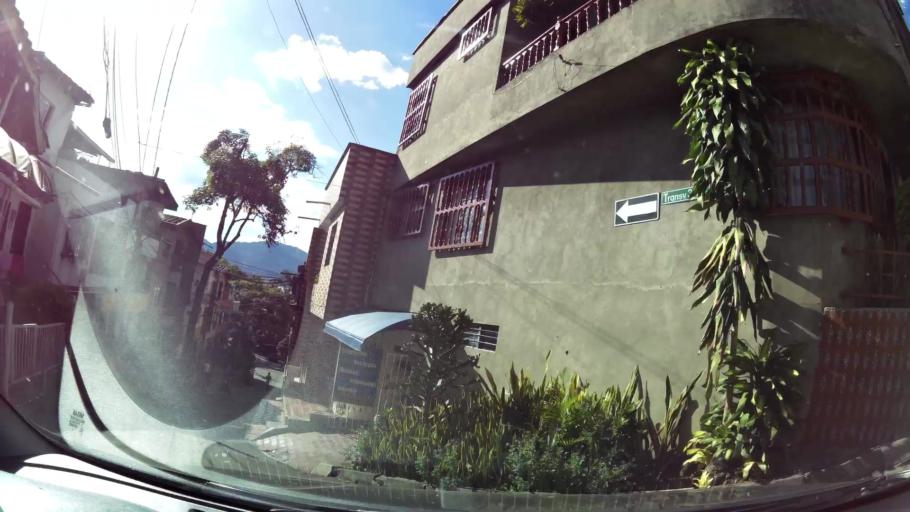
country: CO
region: Antioquia
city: Envigado
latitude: 6.1725
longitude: -75.5782
